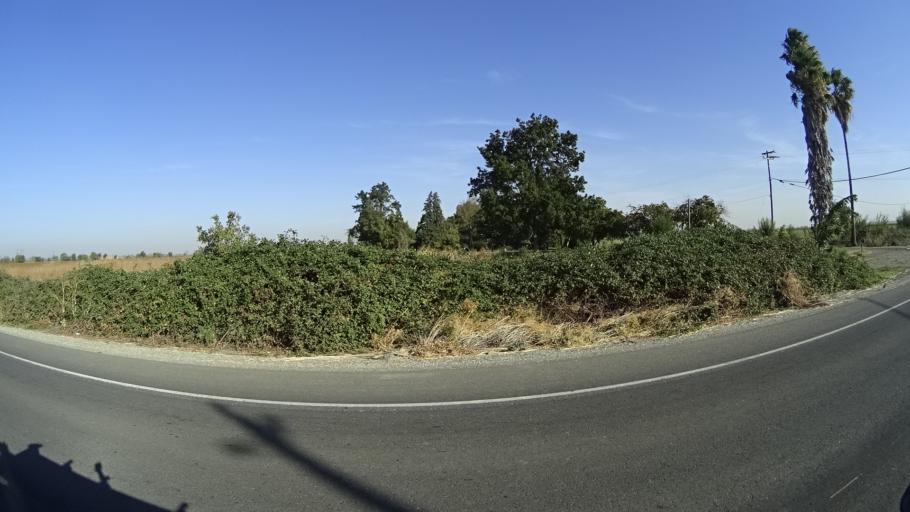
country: US
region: California
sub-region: Sacramento County
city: Parkway
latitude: 38.4140
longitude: -121.5791
